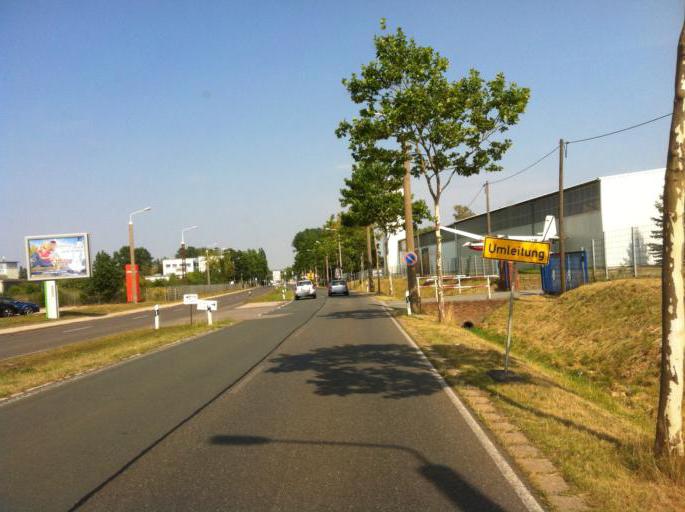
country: DE
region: Saxony
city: Lichtentanne
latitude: 50.7054
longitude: 12.4546
